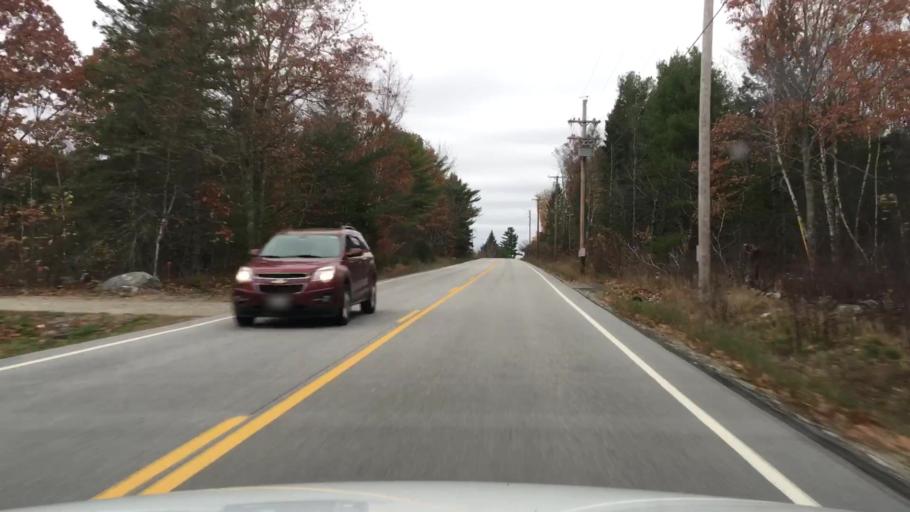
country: US
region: Maine
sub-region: Hancock County
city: Orland
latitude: 44.5444
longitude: -68.6868
